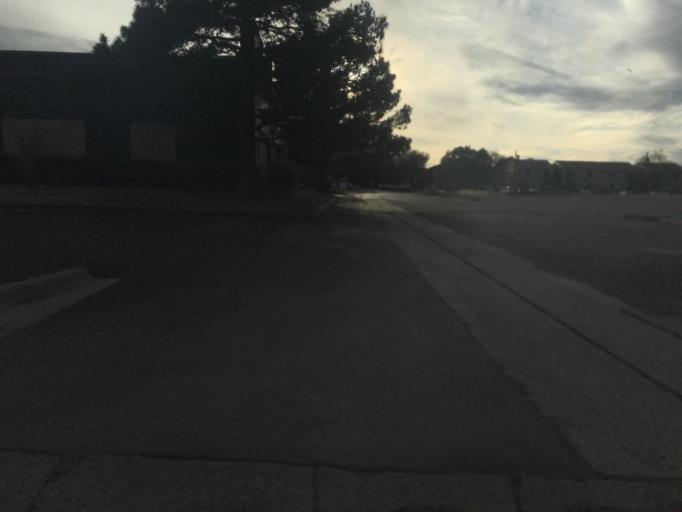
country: US
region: Texas
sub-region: Taylor County
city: Abilene
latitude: 32.4193
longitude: -99.7825
